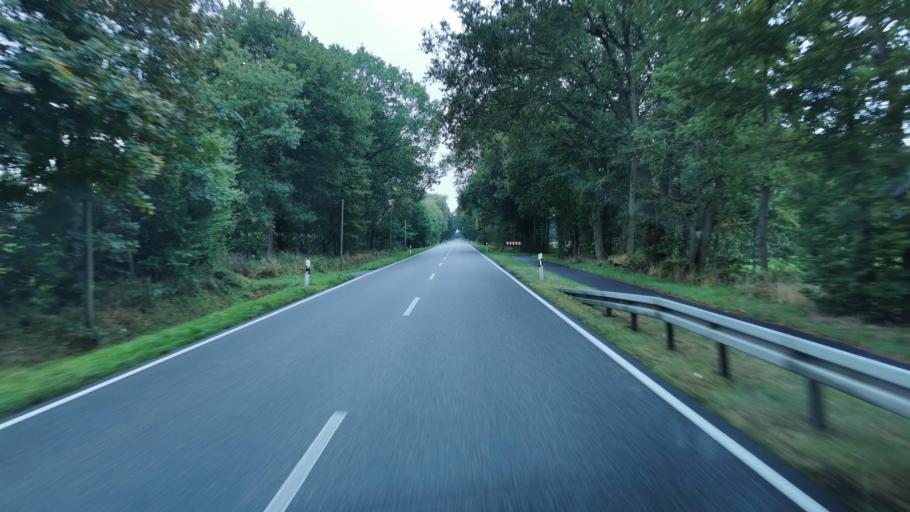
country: DE
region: North Rhine-Westphalia
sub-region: Regierungsbezirk Munster
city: Vreden
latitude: 52.0845
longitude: 6.8543
